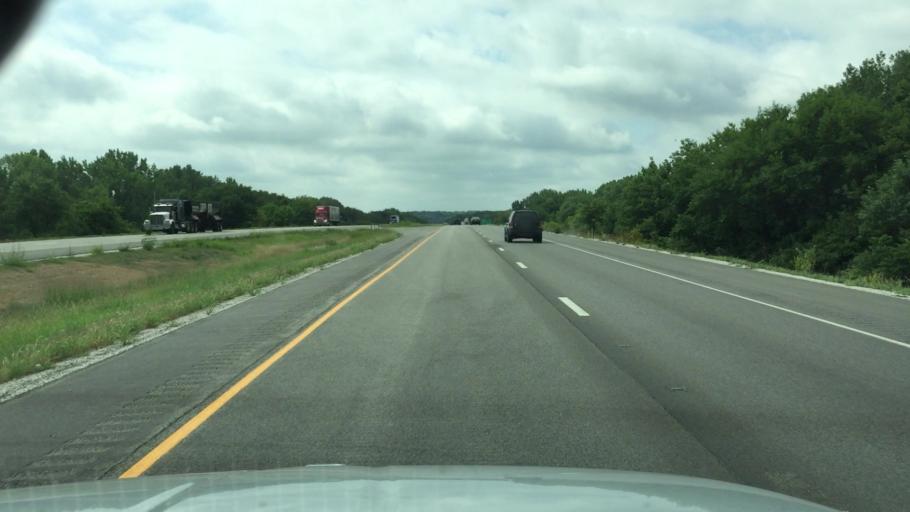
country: US
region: Illinois
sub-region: Henry County
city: Colona
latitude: 41.5238
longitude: -90.3417
